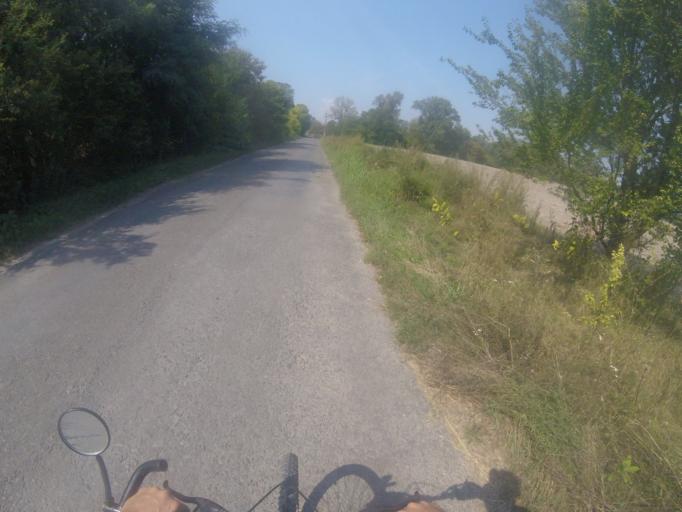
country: HU
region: Bacs-Kiskun
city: Ersekcsanad
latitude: 46.2574
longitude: 18.9239
